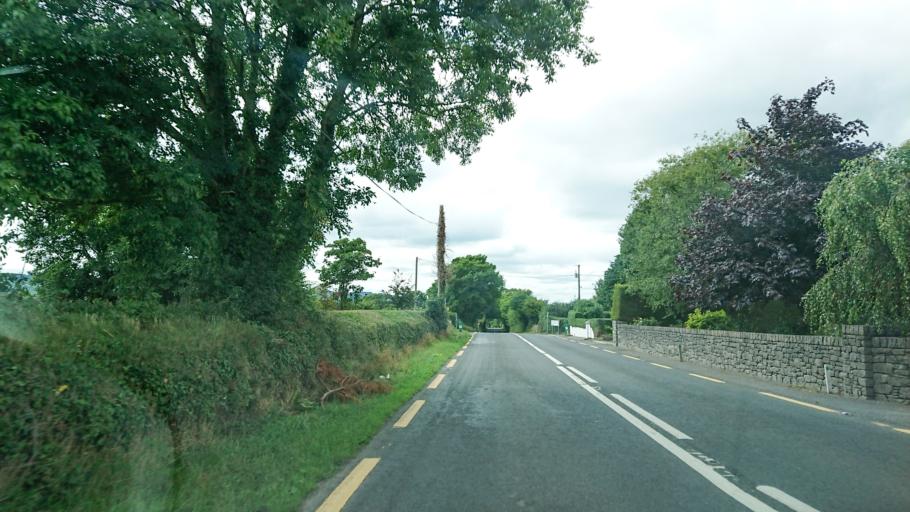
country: IE
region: Munster
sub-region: Waterford
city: Dungarvan
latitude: 52.1087
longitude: -7.6365
